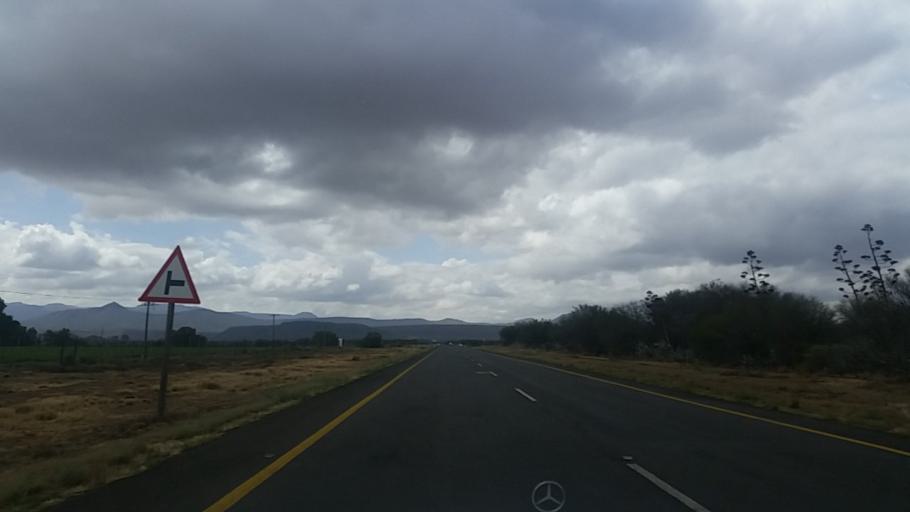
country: ZA
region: Eastern Cape
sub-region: Cacadu District Municipality
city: Graaff-Reinet
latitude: -32.1880
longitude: 24.5589
